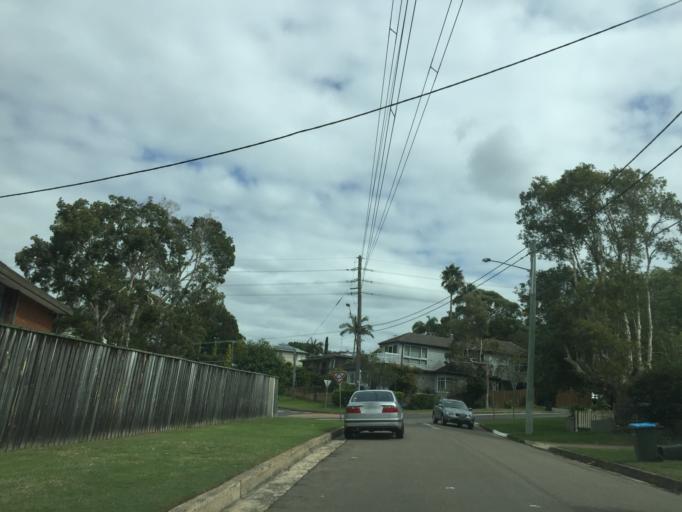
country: AU
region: New South Wales
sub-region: Pittwater
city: North Narrabeen
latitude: -33.7010
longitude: 151.2806
